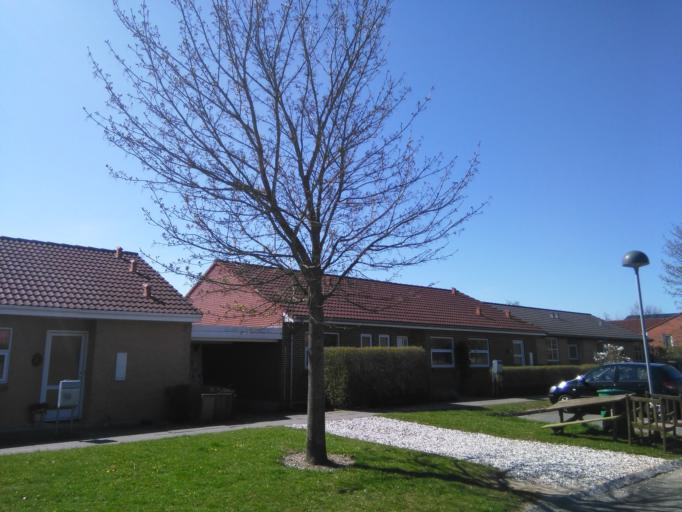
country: DK
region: Central Jutland
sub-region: Arhus Kommune
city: Marslet
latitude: 56.0683
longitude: 10.1717
